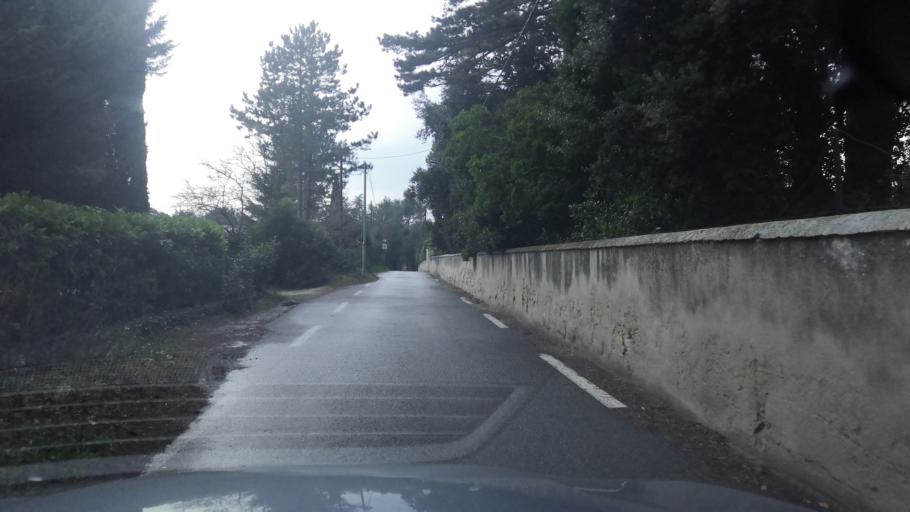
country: FR
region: Provence-Alpes-Cote d'Azur
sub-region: Departement des Bouches-du-Rhone
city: Aix-en-Provence
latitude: 43.5614
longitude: 5.4150
